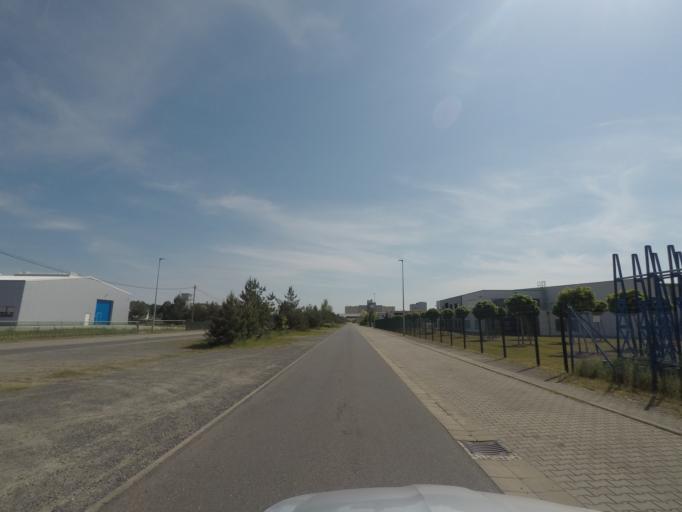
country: DE
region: Brandenburg
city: Britz
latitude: 52.8583
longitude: 13.7881
